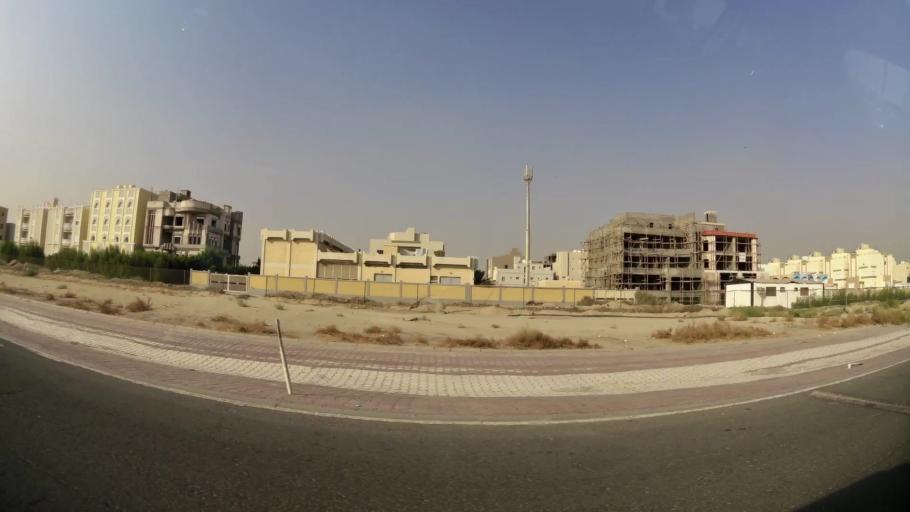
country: KW
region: Mubarak al Kabir
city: Mubarak al Kabir
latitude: 29.1949
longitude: 48.1085
